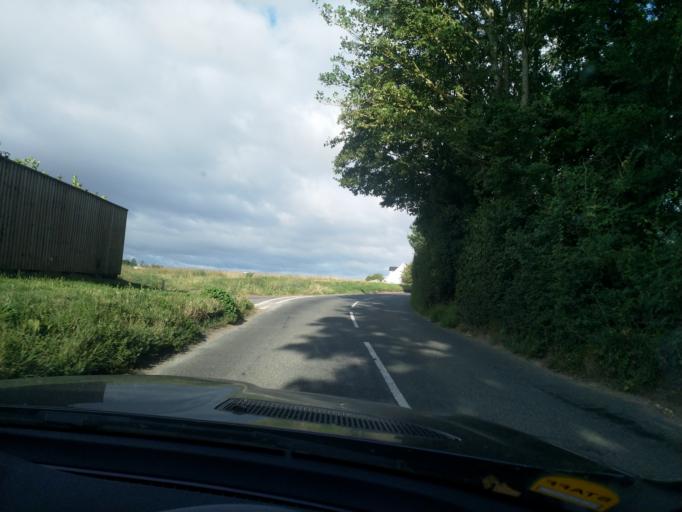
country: GB
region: England
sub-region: Suffolk
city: Elmswell
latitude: 52.2298
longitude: 0.9289
